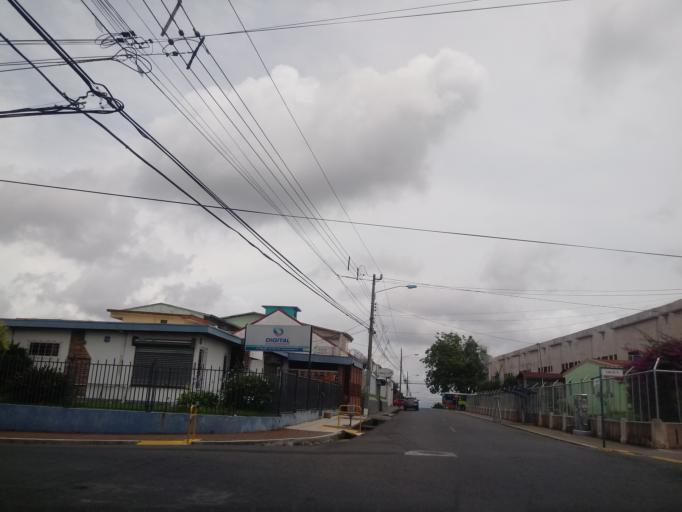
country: CR
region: Heredia
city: Heredia
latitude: 10.0020
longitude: -84.1149
